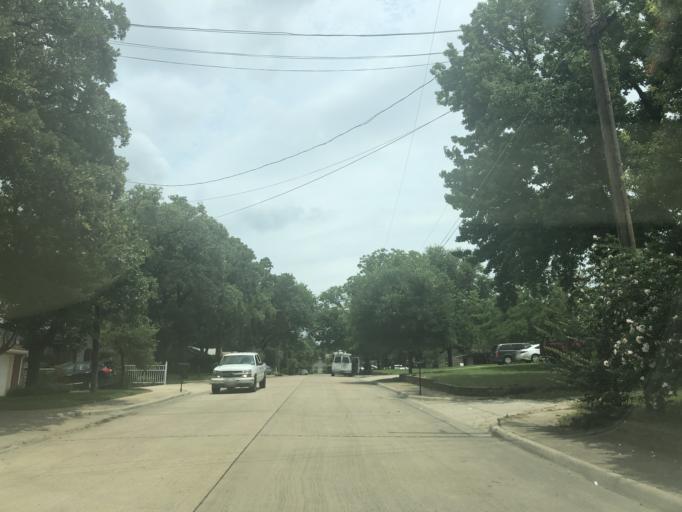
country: US
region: Texas
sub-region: Dallas County
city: Irving
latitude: 32.7992
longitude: -96.9385
